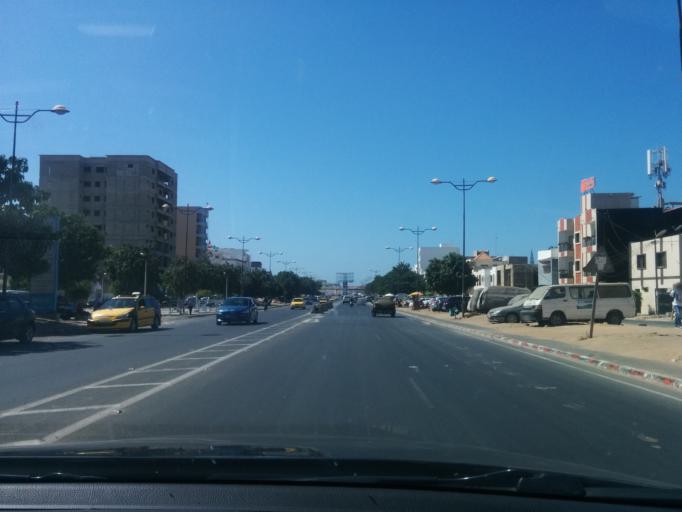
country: SN
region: Dakar
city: Mermoz Boabab
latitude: 14.7172
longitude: -17.4680
